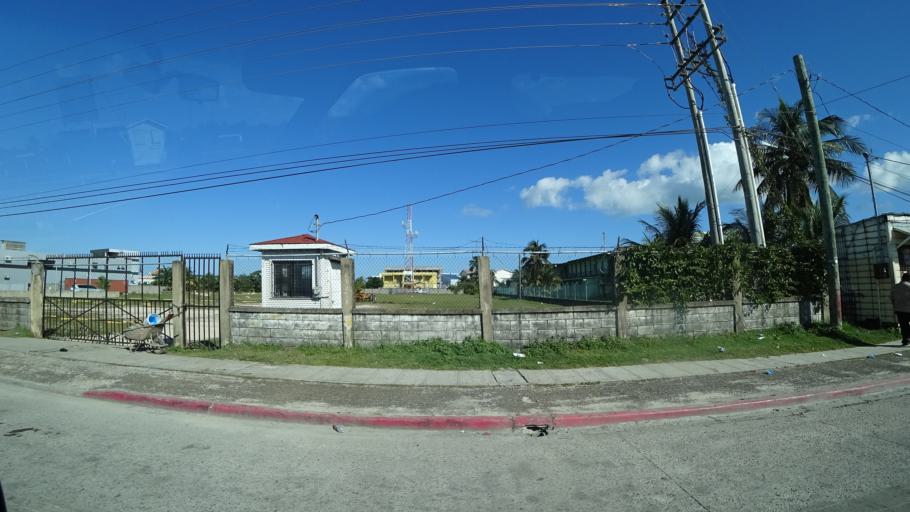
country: BZ
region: Belize
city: Belize City
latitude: 17.5042
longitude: -88.1976
